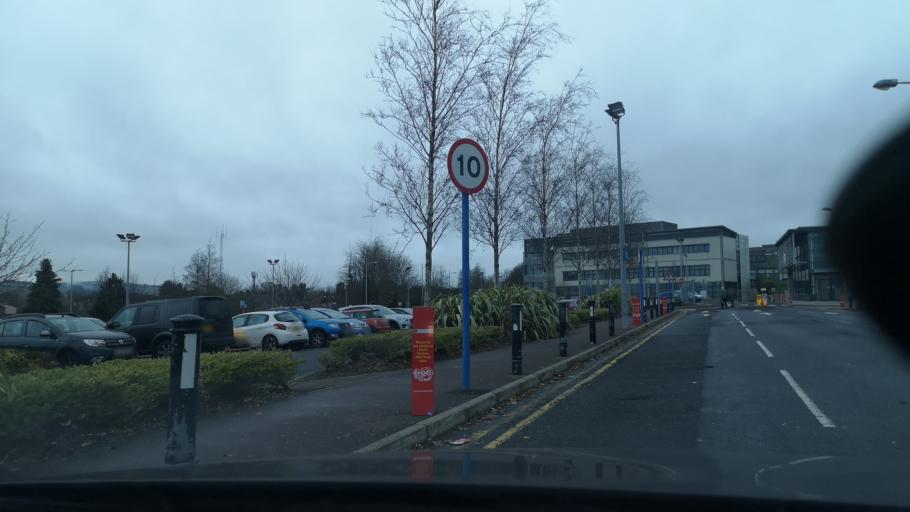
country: GB
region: Northern Ireland
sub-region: Castlereagh District
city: Dundonald
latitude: 54.5958
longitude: -5.8100
